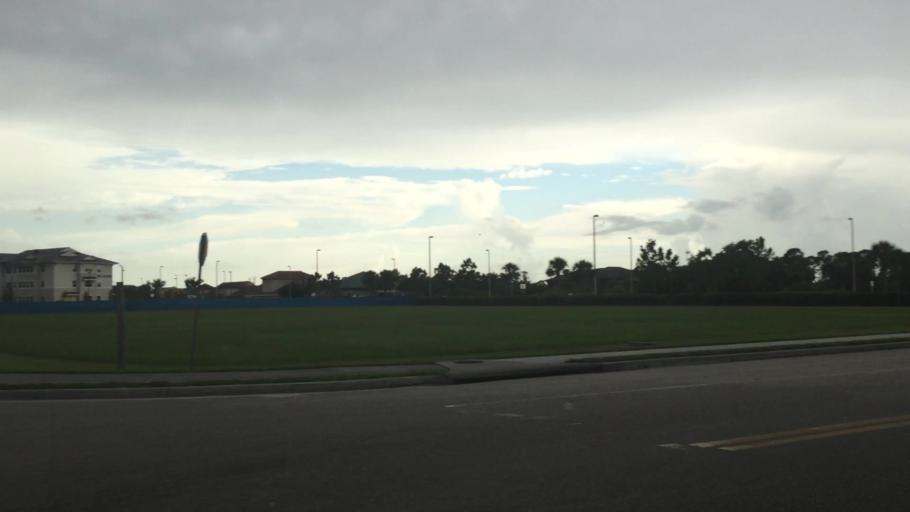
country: US
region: Florida
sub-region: Lee County
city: Villas
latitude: 26.5411
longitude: -81.8516
